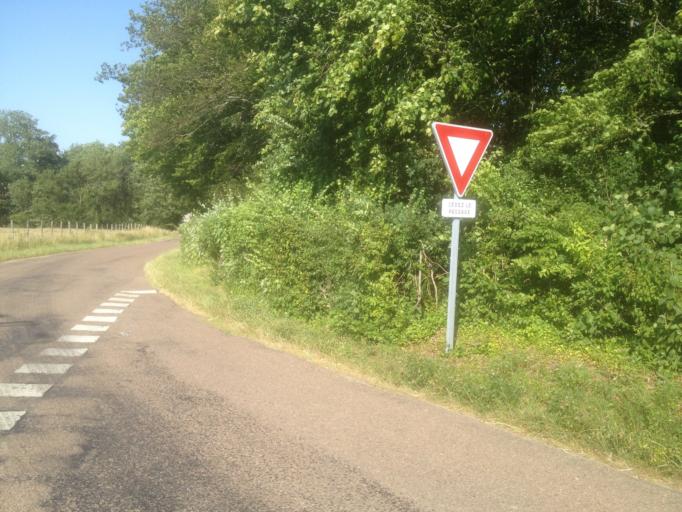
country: FR
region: Champagne-Ardenne
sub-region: Departement de la Haute-Marne
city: Joinville
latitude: 48.4604
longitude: 5.3048
